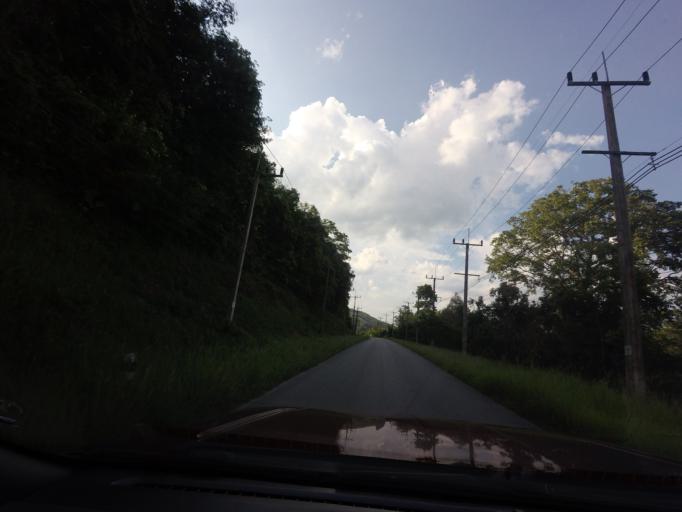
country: TH
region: Yala
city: Ban Nang Sata
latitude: 6.1916
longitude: 101.2600
